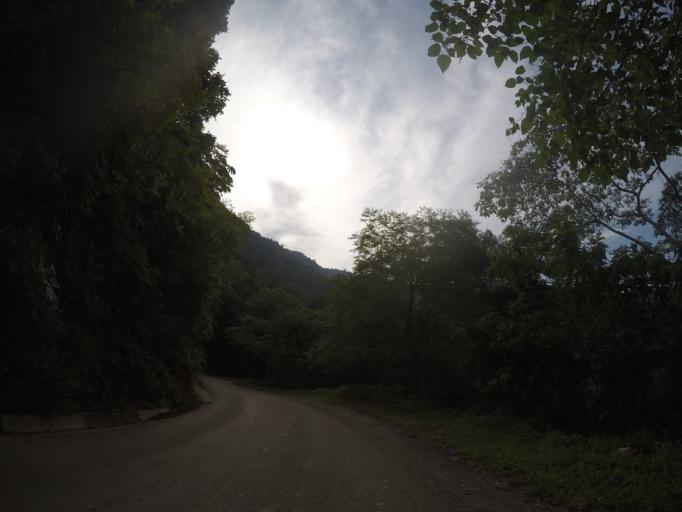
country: MX
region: Oaxaca
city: Pluma Hidalgo
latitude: 15.9496
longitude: -96.4429
